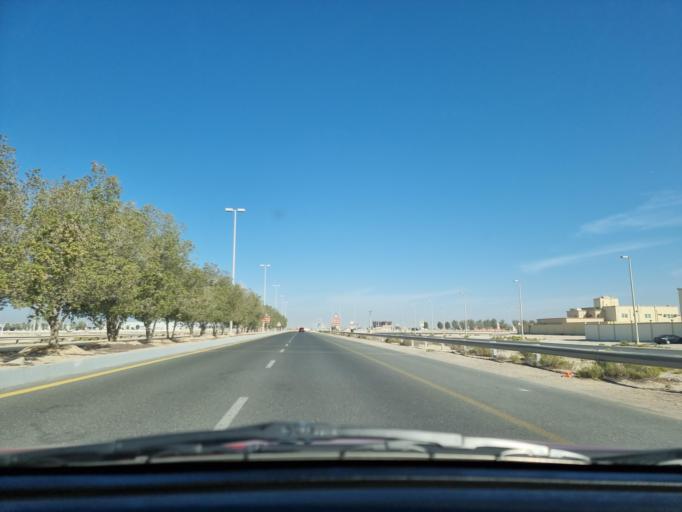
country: AE
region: Abu Dhabi
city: Abu Dhabi
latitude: 24.3953
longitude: 54.6940
